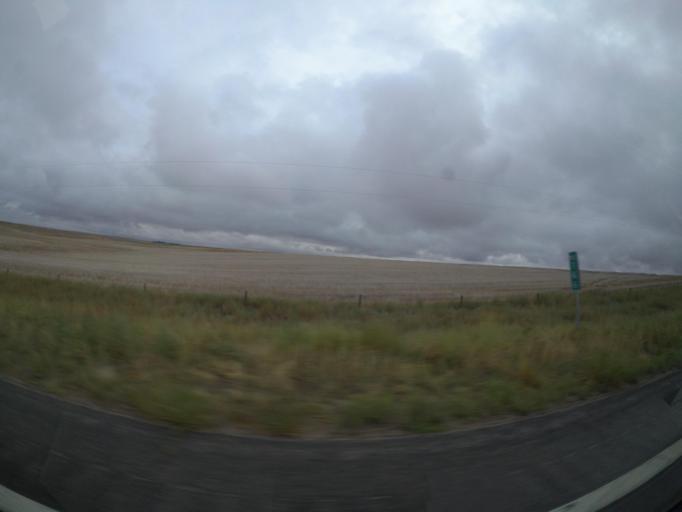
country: US
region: Colorado
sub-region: Washington County
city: Akron
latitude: 39.6991
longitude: -103.0442
